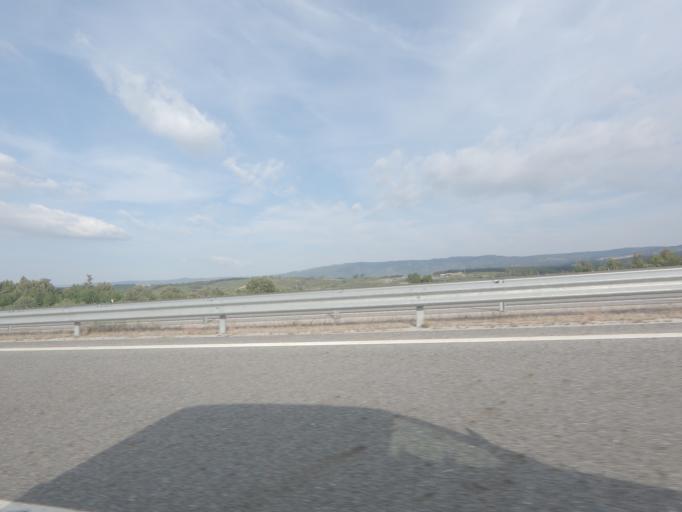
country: PT
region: Vila Real
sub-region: Chaves
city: Chaves
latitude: 41.7311
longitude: -7.5323
